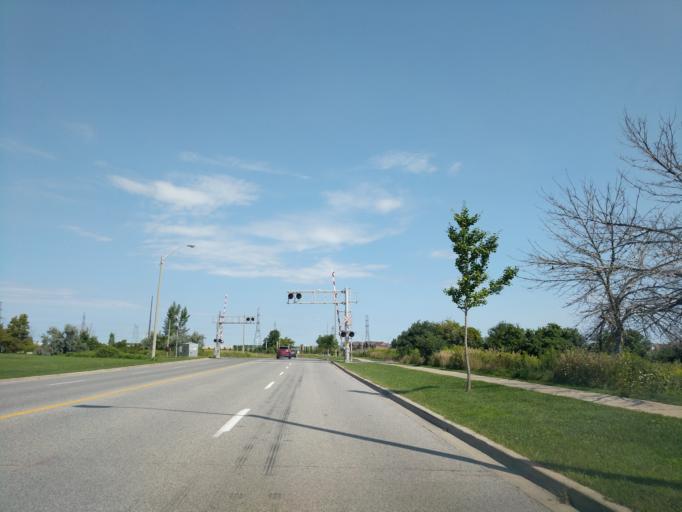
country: CA
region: Ontario
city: Scarborough
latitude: 43.8206
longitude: -79.2300
